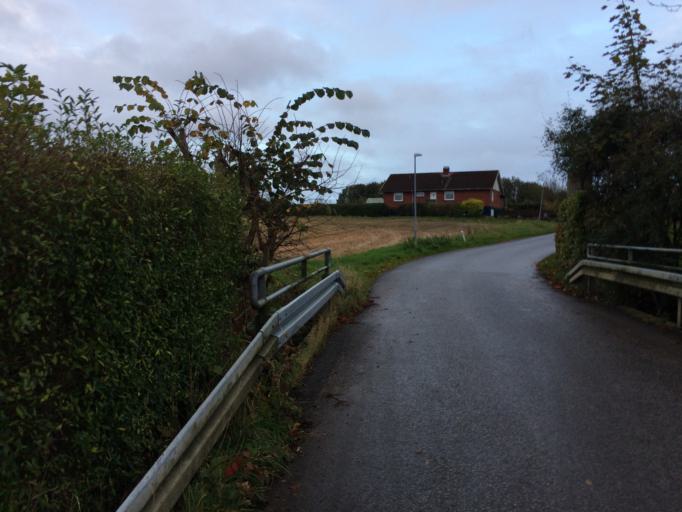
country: DK
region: South Denmark
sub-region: Vejle Kommune
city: Borkop
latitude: 55.6076
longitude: 9.6462
